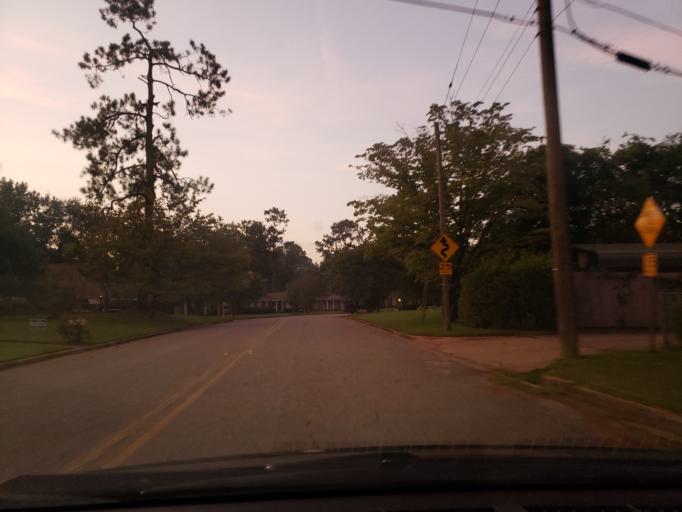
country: US
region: Georgia
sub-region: Dougherty County
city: Albany
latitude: 31.5868
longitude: -84.2042
